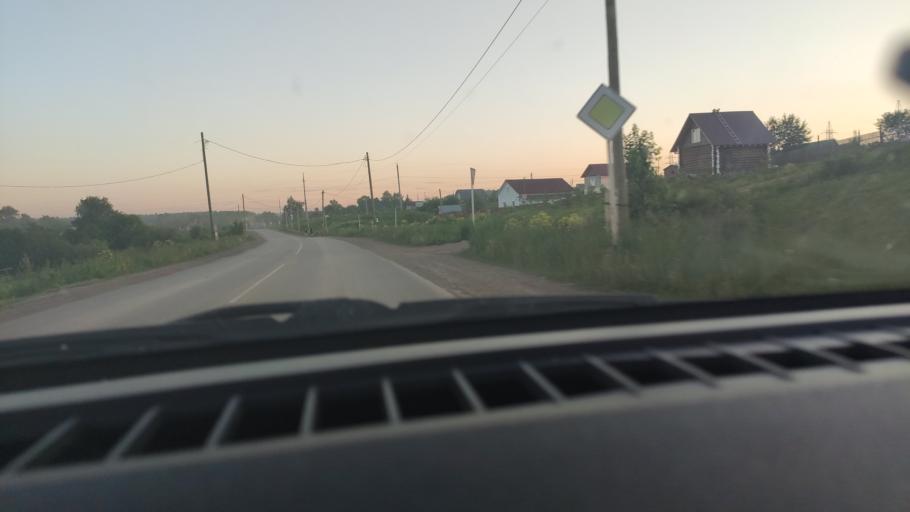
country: RU
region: Perm
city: Kultayevo
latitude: 57.8976
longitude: 55.9187
